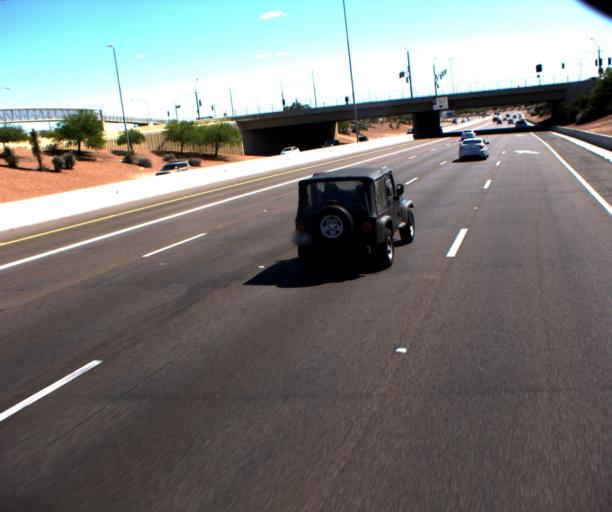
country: US
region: Arizona
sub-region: Maricopa County
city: Paradise Valley
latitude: 33.6419
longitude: -112.0027
